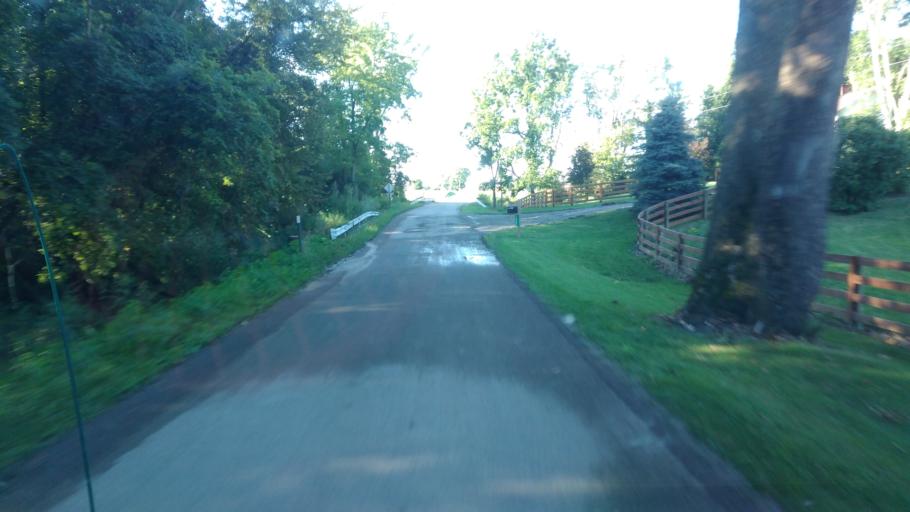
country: US
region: Ohio
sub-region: Wyandot County
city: Upper Sandusky
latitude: 40.8115
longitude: -83.3808
